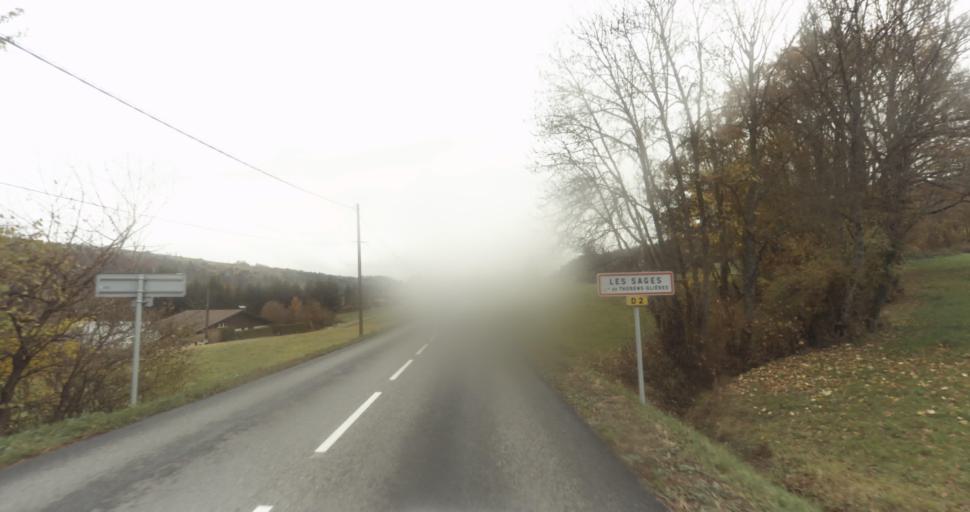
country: FR
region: Rhone-Alpes
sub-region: Departement de la Haute-Savoie
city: Thorens-Glieres
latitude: 45.9983
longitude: 6.2225
